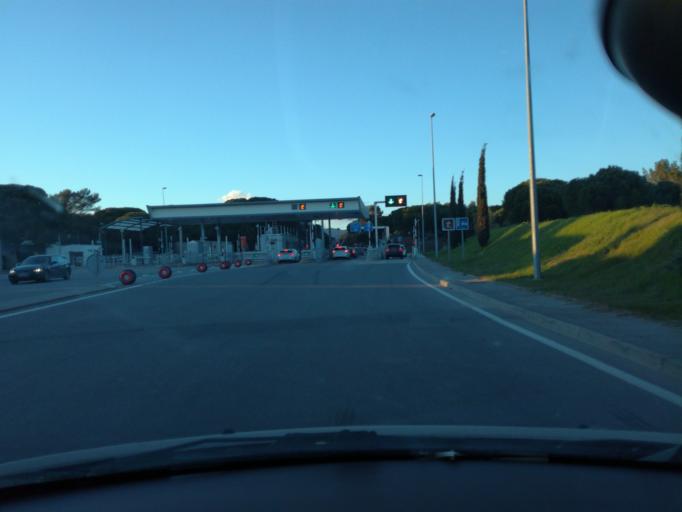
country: FR
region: Provence-Alpes-Cote d'Azur
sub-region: Departement du Var
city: Puget-sur-Argens
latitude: 43.4563
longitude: 6.6899
